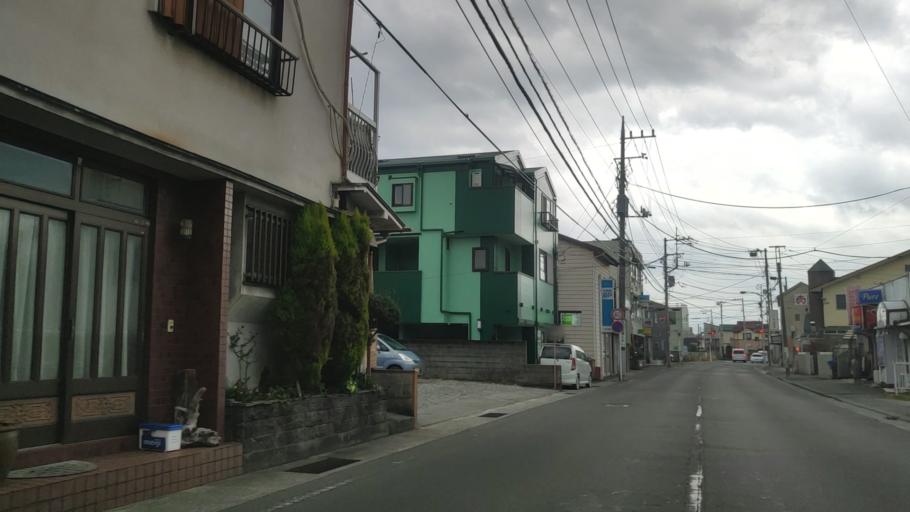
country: JP
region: Kanagawa
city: Odawara
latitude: 35.2586
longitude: 139.1632
